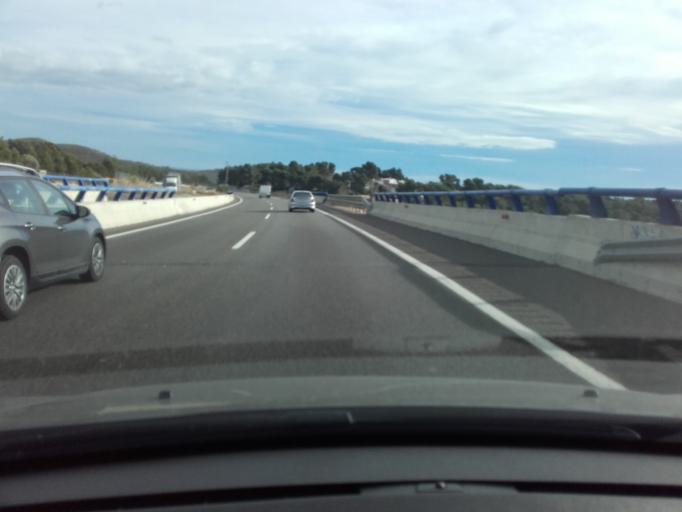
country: ES
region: Catalonia
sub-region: Provincia de Tarragona
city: el Catllar
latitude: 41.1458
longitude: 1.3139
